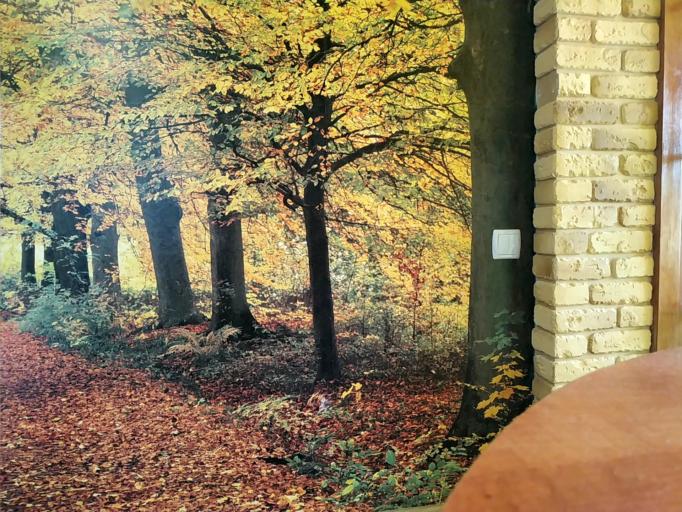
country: RU
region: Pskov
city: Dno
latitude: 57.9120
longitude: 30.1714
